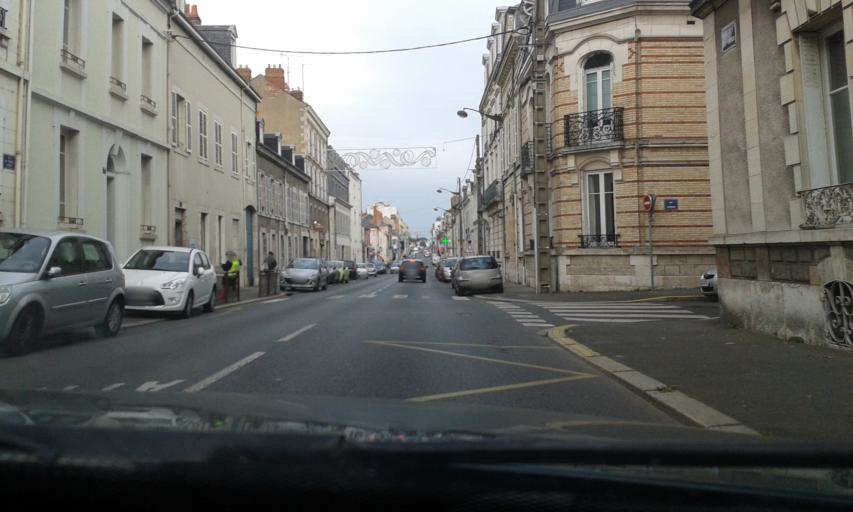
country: FR
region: Centre
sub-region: Departement du Loiret
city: Orleans
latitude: 47.9114
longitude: 1.9003
